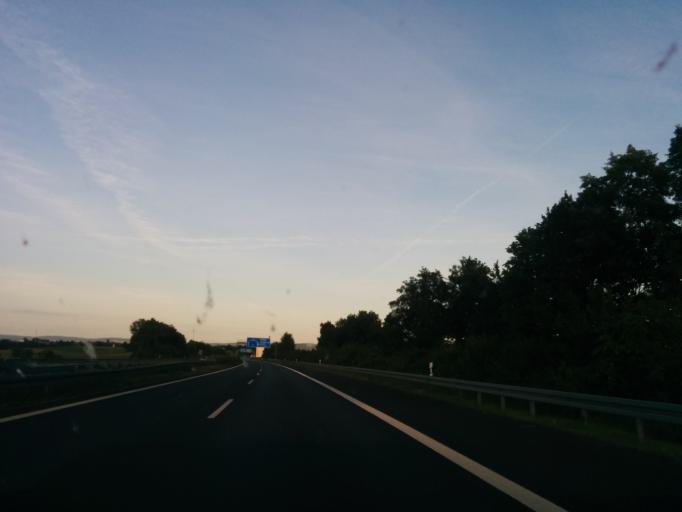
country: DE
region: Bavaria
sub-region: Regierungsbezirk Unterfranken
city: Biebelried
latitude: 49.7897
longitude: 10.0687
